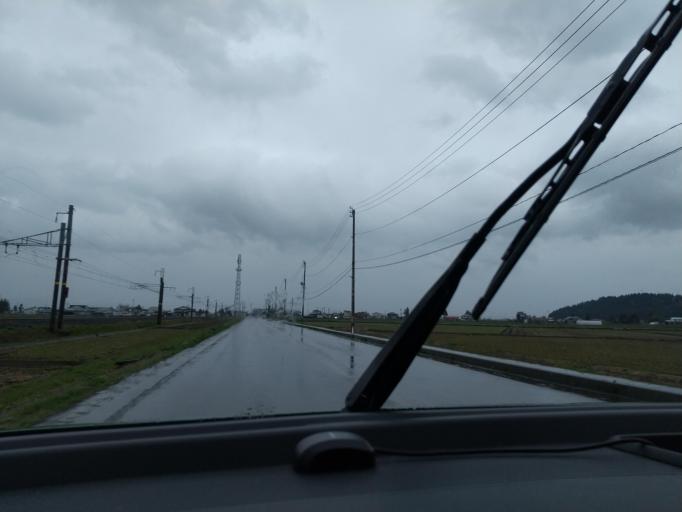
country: JP
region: Akita
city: Yokotemachi
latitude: 39.3695
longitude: 140.5361
